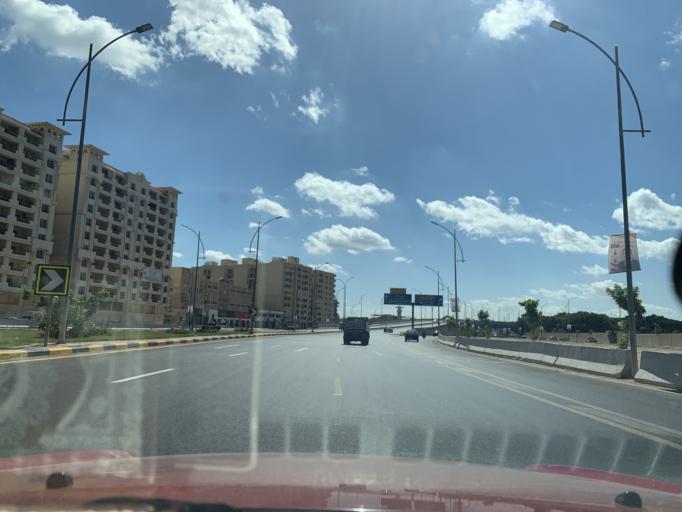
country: EG
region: Alexandria
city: Alexandria
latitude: 31.2034
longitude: 29.9539
